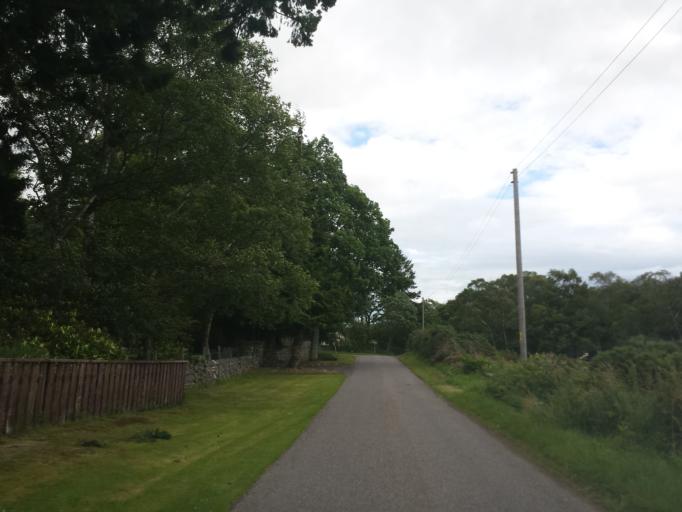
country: GB
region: Scotland
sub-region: Highland
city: Fortrose
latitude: 57.5116
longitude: -4.0207
